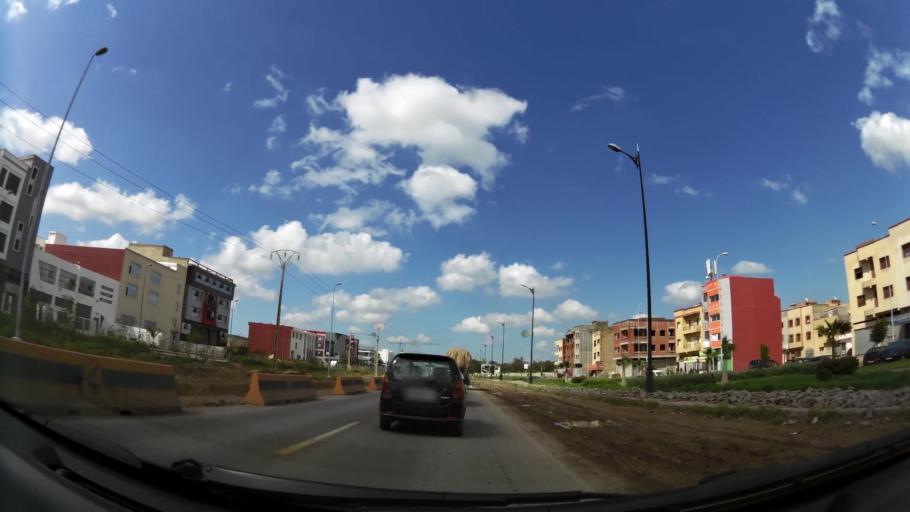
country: MA
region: Grand Casablanca
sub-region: Mediouna
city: Mediouna
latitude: 33.4003
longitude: -7.5345
